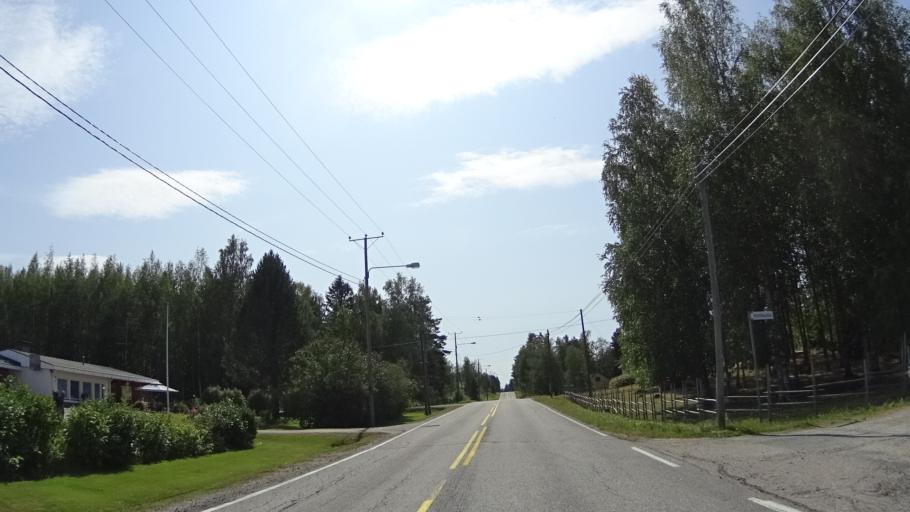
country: FI
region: Pirkanmaa
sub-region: Ylae-Pirkanmaa
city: Maenttae
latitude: 61.8930
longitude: 24.7928
